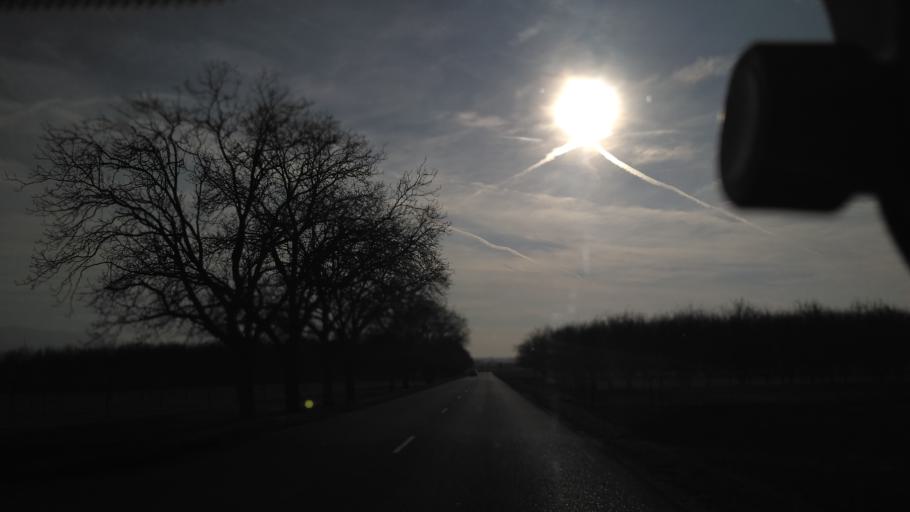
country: FR
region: Rhone-Alpes
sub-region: Departement de la Drome
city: Saint-Paul-les-Romans
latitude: 45.0837
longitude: 5.1346
